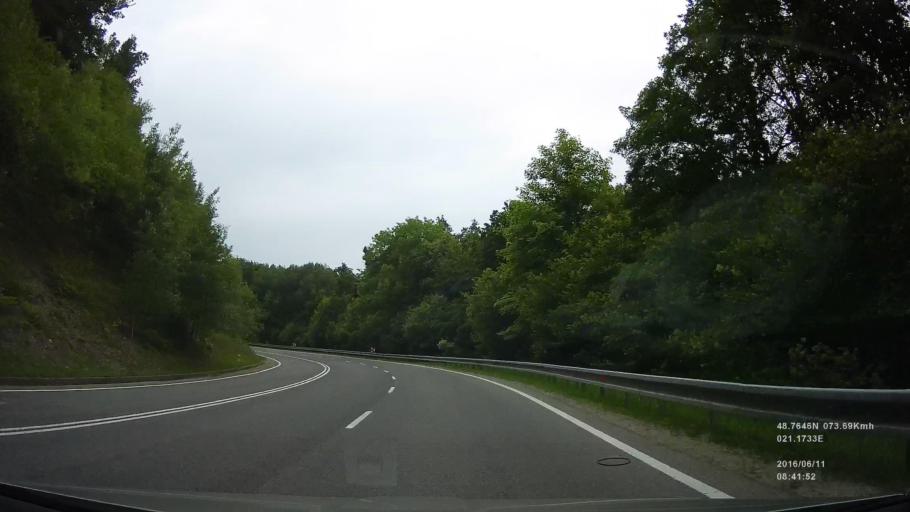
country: SK
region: Kosicky
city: Kosice
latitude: 48.7611
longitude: 21.1775
